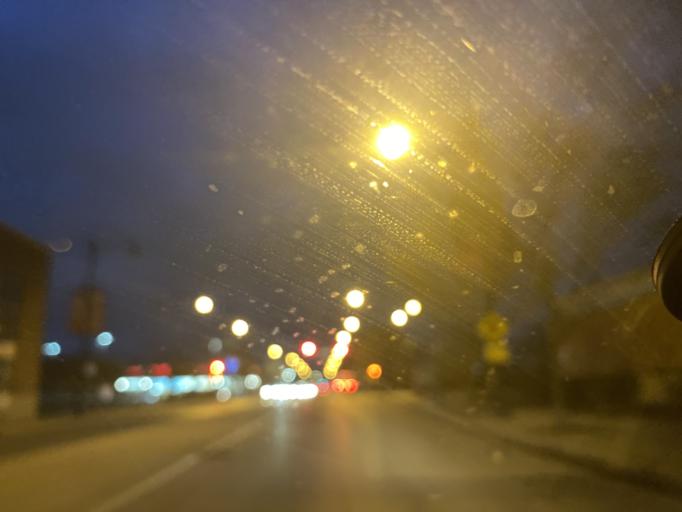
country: US
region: Illinois
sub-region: Cook County
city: Chicago
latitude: 41.7798
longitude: -87.6434
